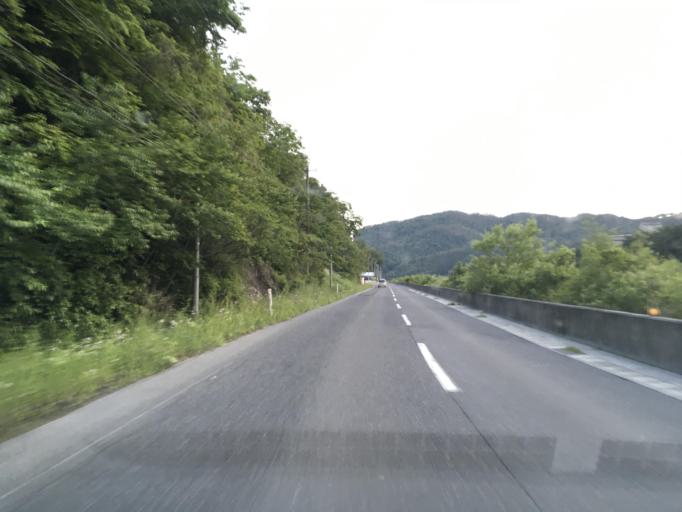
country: JP
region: Iwate
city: Ichinoseki
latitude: 38.9841
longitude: 141.2496
